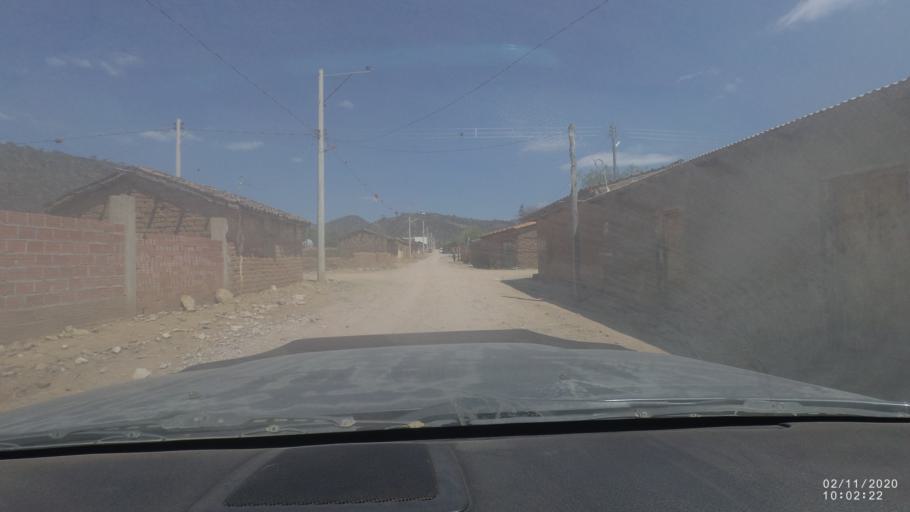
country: BO
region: Chuquisaca
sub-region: Provincia Zudanez
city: Mojocoya
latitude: -18.3246
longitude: -64.6720
